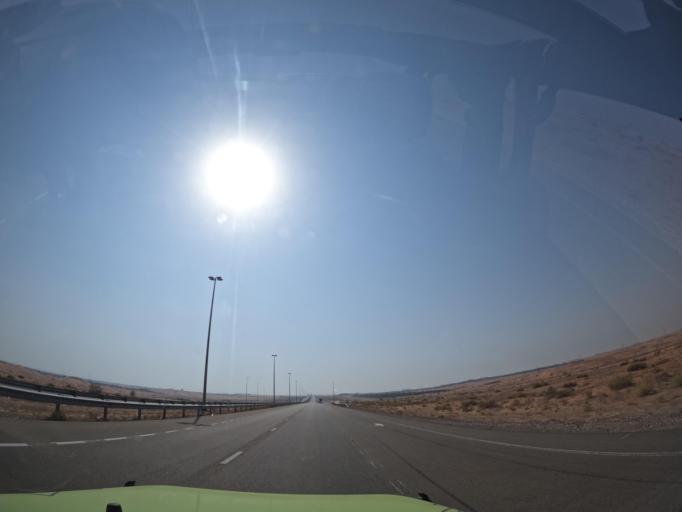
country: OM
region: Al Buraimi
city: Al Buraymi
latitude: 24.4114
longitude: 55.7009
